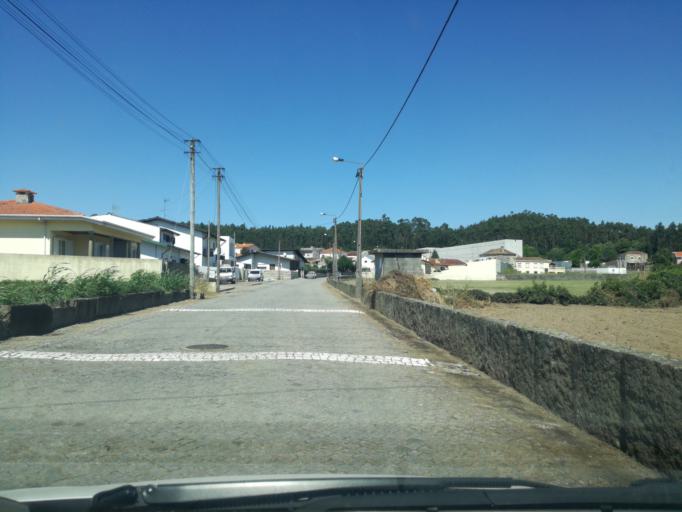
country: PT
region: Porto
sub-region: Maia
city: Gemunde
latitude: 41.2748
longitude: -8.6364
